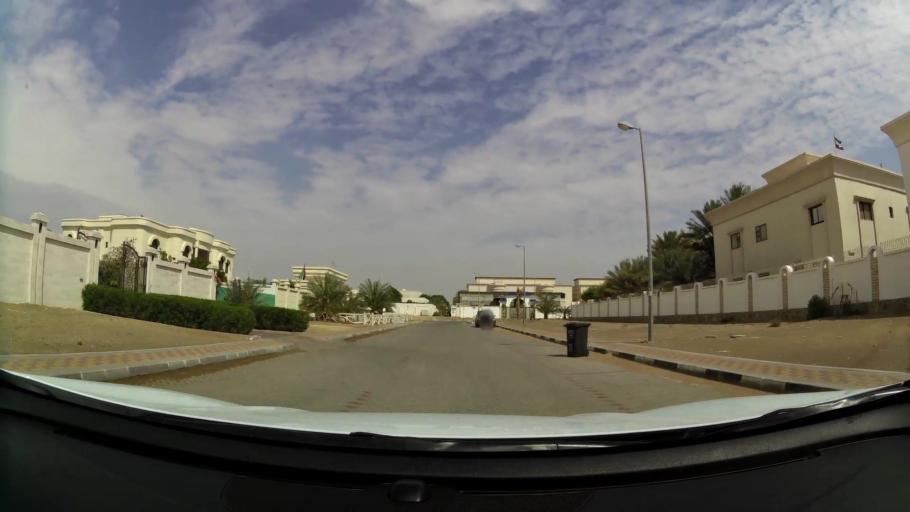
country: AE
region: Abu Dhabi
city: Al Ain
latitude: 24.1899
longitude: 55.7928
